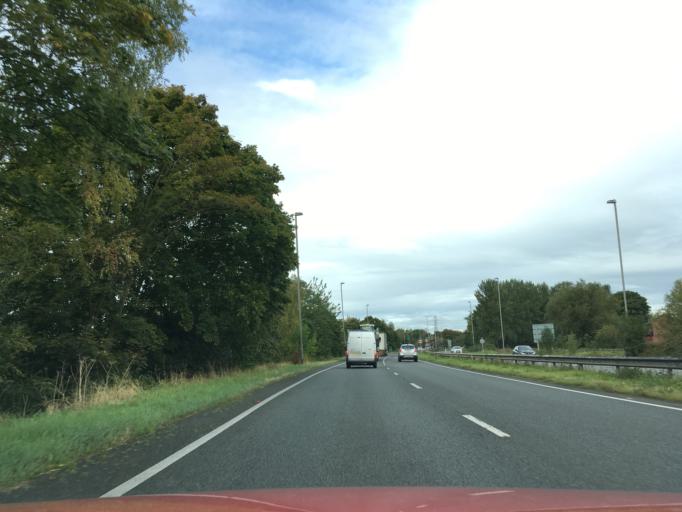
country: GB
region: England
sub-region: Gloucestershire
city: Gloucester
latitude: 51.8816
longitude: -2.2339
